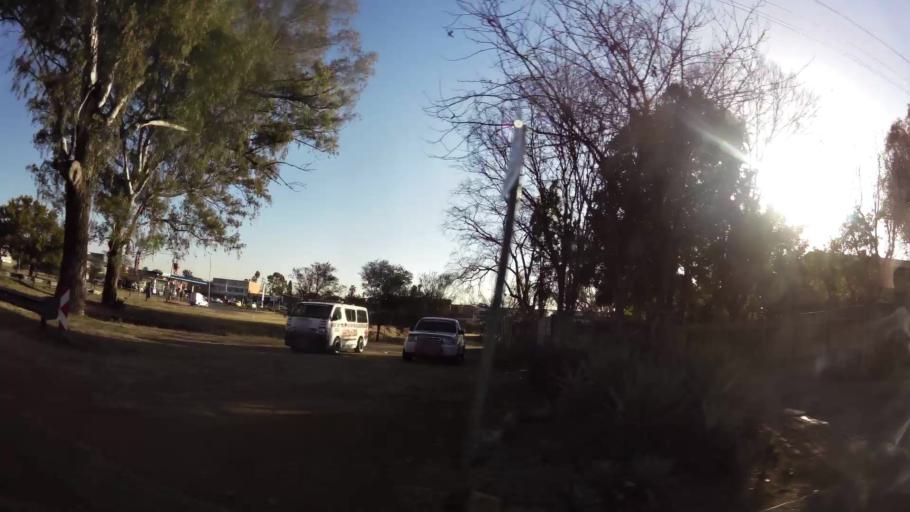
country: ZA
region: Gauteng
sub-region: City of Tshwane Metropolitan Municipality
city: Pretoria
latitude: -25.7068
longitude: 28.2021
